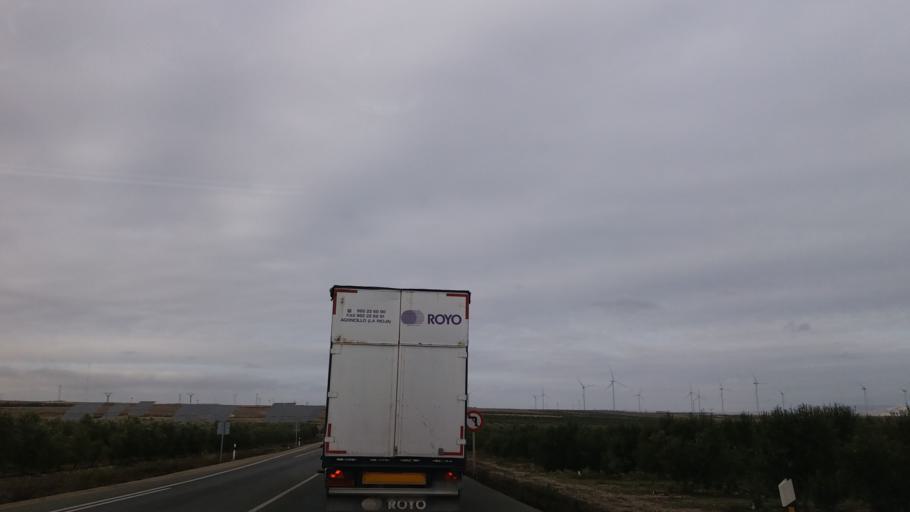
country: ES
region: Aragon
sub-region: Provincia de Zaragoza
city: Mallen
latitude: 41.8574
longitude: -1.3779
